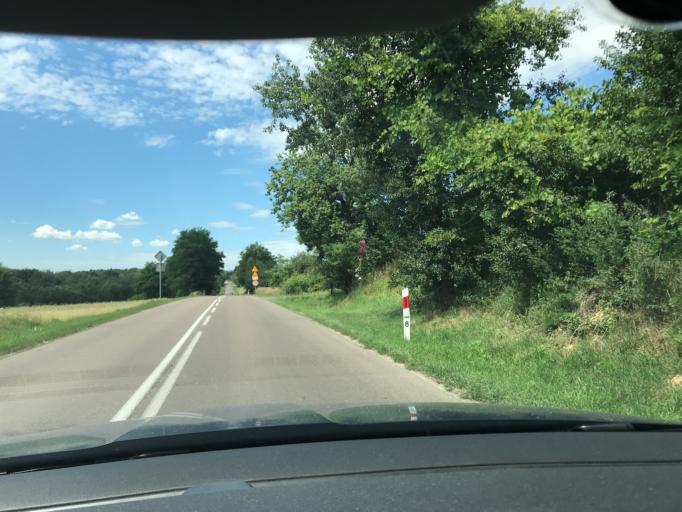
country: PL
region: Lublin Voivodeship
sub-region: Powiat zamojski
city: Szczebrzeszyn
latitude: 50.7169
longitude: 22.9305
